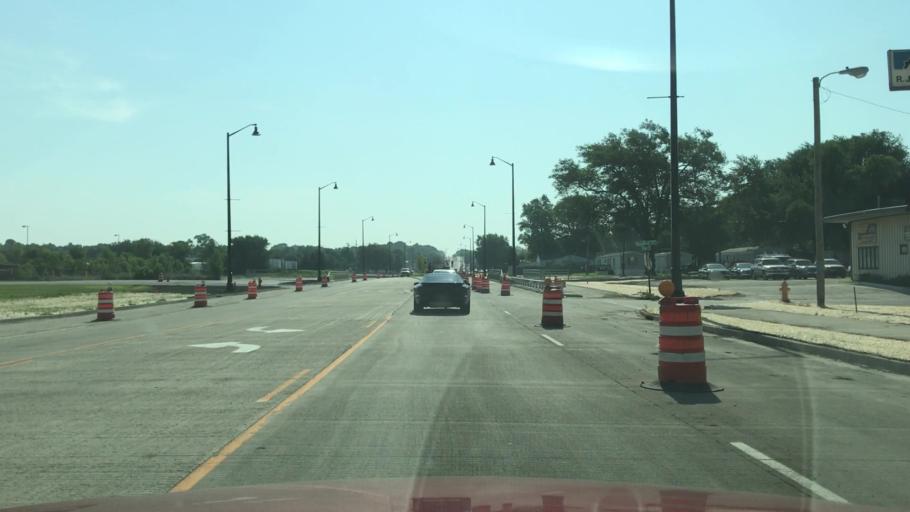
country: US
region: Illinois
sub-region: Winnebago County
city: Rockford
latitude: 42.2379
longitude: -89.0661
